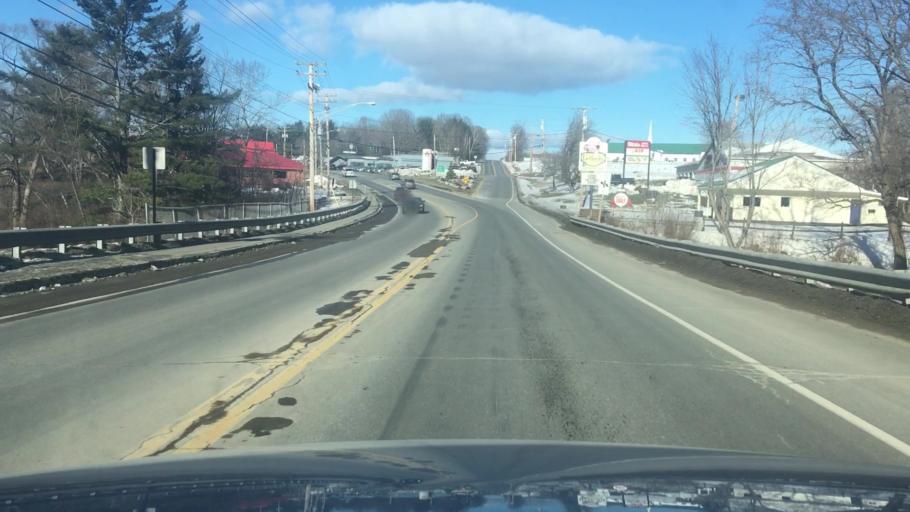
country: US
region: Maine
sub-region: Somerset County
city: Skowhegan
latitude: 44.7820
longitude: -69.7271
